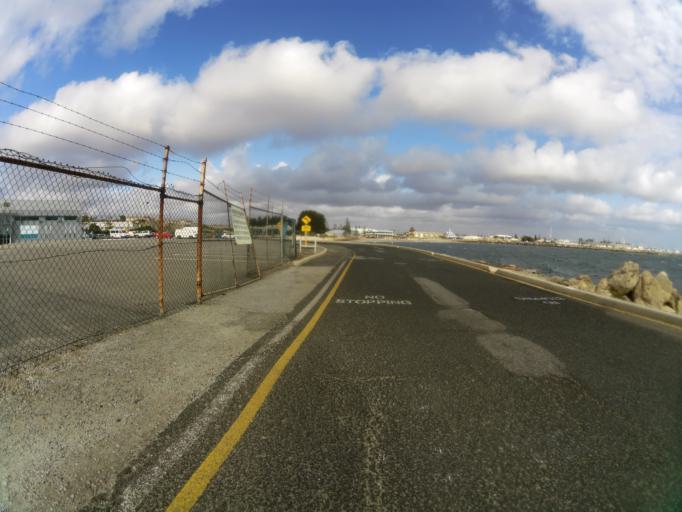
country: AU
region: Western Australia
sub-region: Fremantle
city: South Fremantle
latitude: -32.0566
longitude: 115.7387
